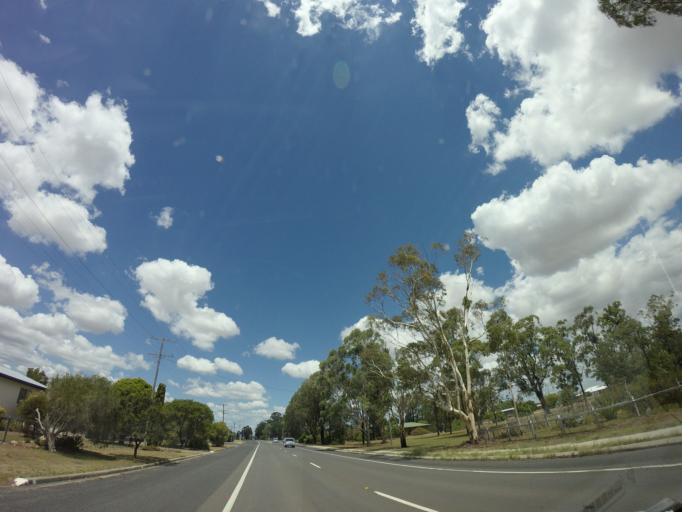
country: AU
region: Queensland
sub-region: Toowoomba
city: Oakey
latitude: -27.8775
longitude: 151.2603
